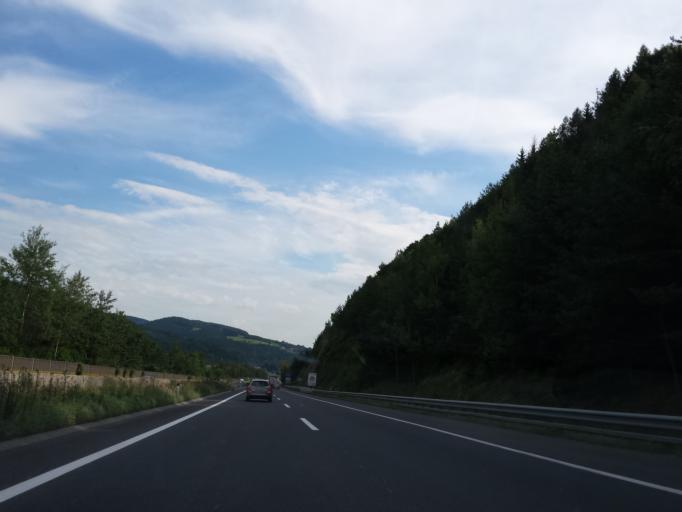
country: AT
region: Lower Austria
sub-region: Politischer Bezirk Neunkirchen
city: Warth
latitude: 47.6426
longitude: 16.1247
